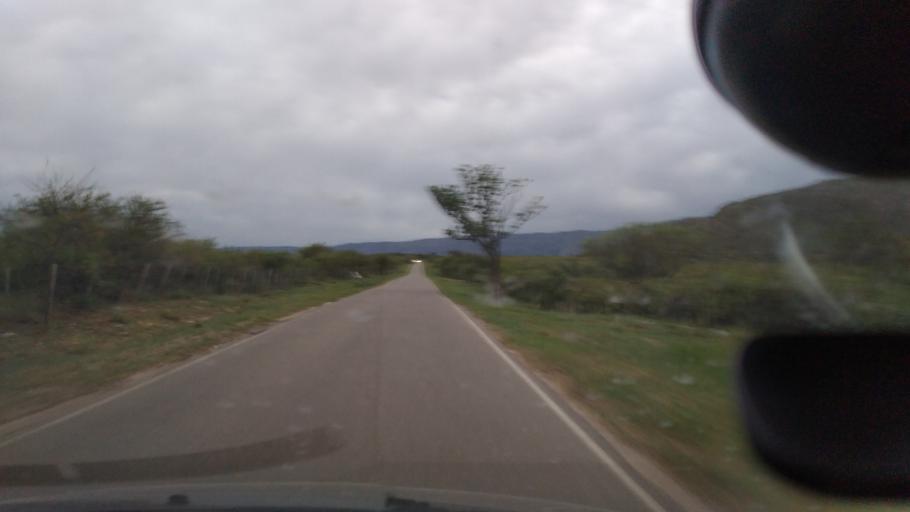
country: AR
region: Cordoba
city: Villa Las Rosas
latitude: -31.8881
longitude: -65.0297
